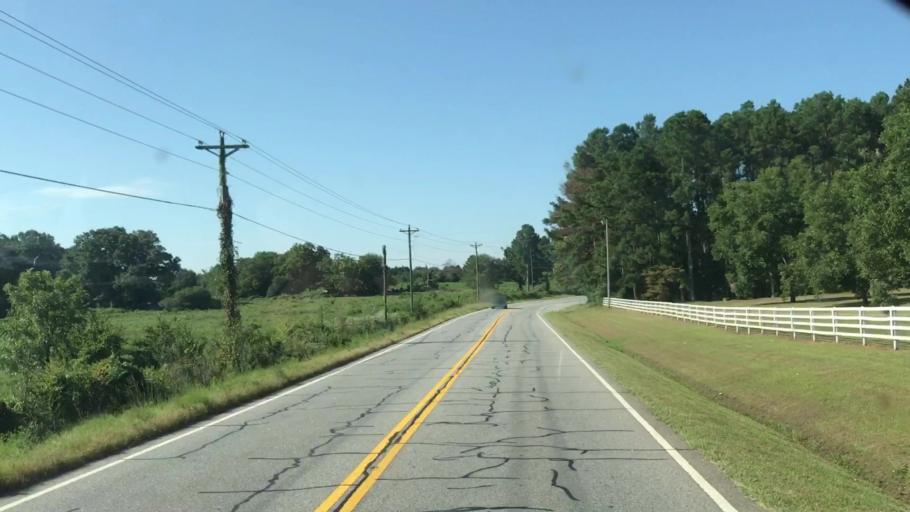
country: US
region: Georgia
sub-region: Walton County
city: Loganville
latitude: 33.8883
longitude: -83.8101
